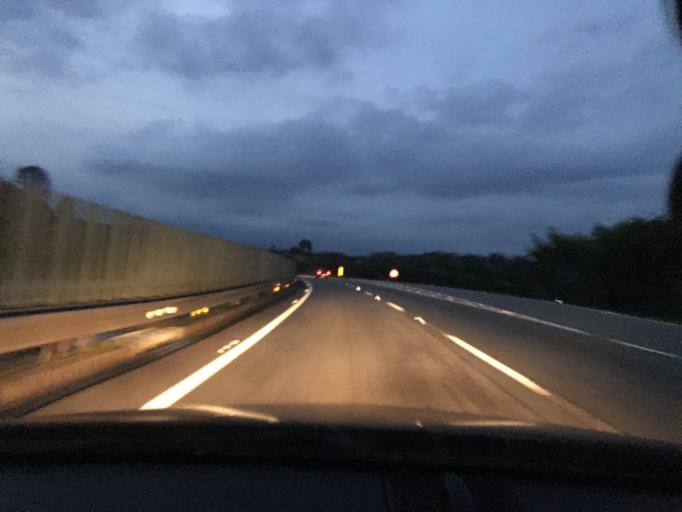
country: BR
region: Sao Paulo
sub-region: Santa Isabel
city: Santa Isabel
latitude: -23.3425
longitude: -46.1273
